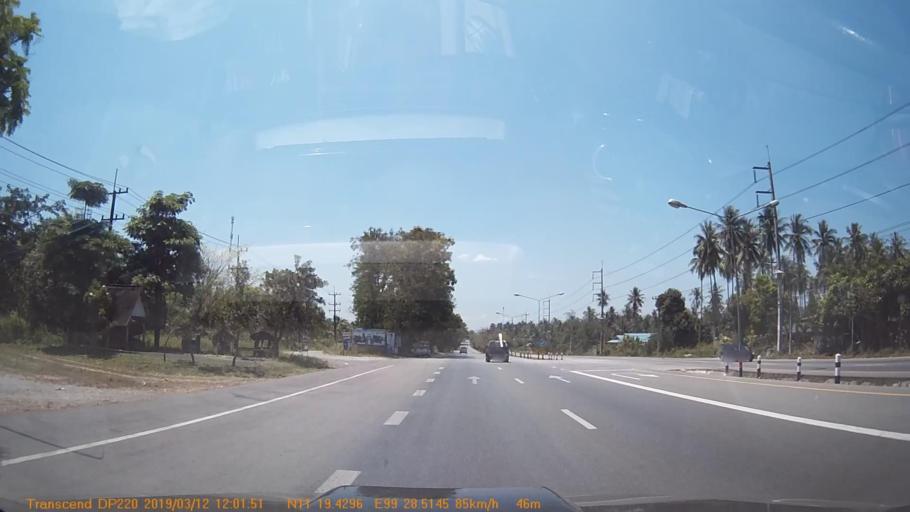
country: TH
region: Prachuap Khiri Khan
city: Bang Saphan
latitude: 11.3238
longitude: 99.4752
